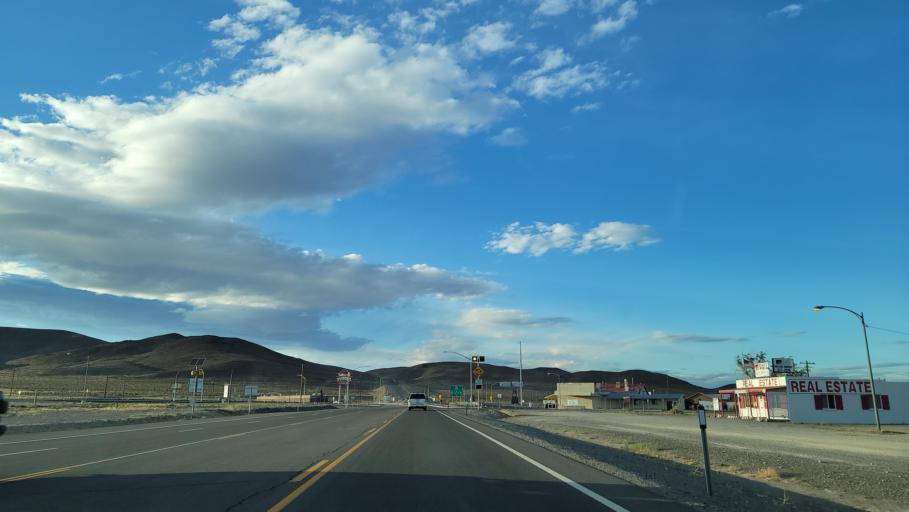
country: US
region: Nevada
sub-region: Lyon County
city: Silver Springs
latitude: 39.4137
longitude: -119.2255
